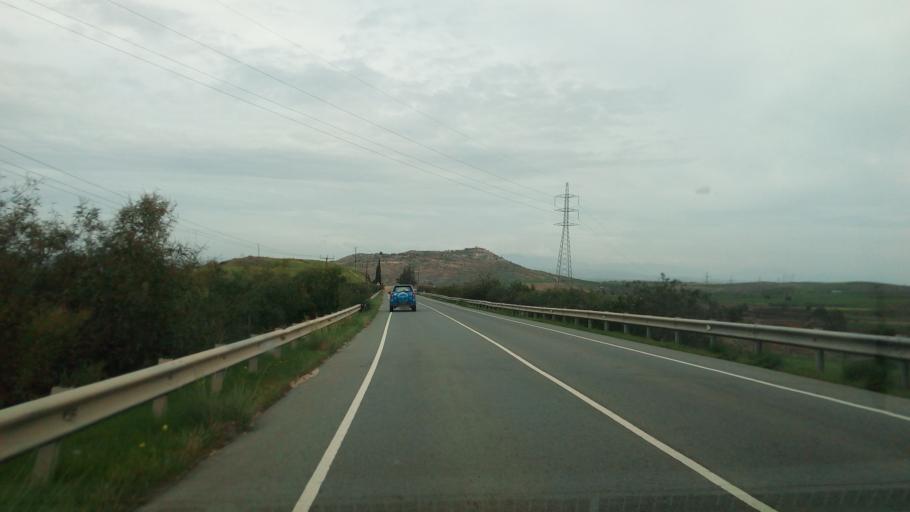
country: CY
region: Lefkosia
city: Kakopetria
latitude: 35.0780
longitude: 32.9478
